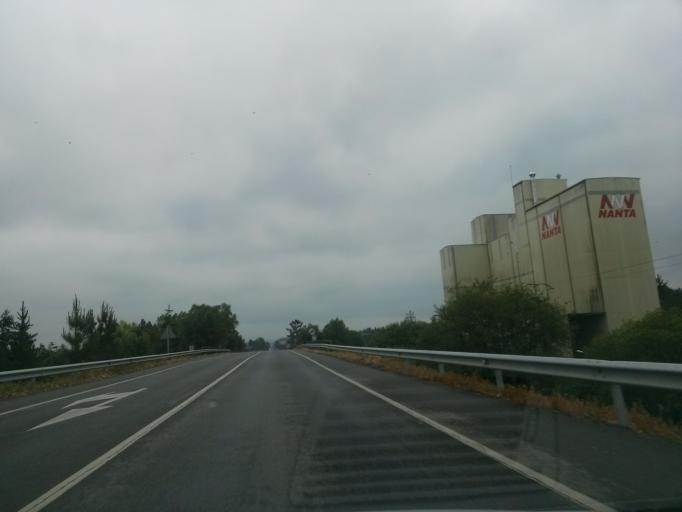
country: ES
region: Galicia
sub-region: Provincia de Lugo
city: Rabade
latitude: 43.1285
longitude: -7.6446
